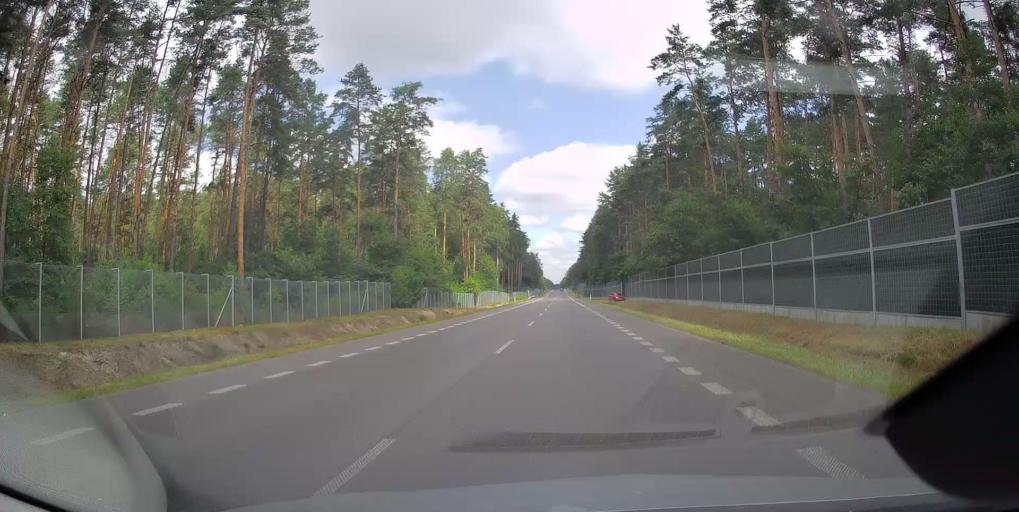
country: PL
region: Subcarpathian Voivodeship
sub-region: Powiat mielecki
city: Mielec
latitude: 50.2681
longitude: 21.4948
